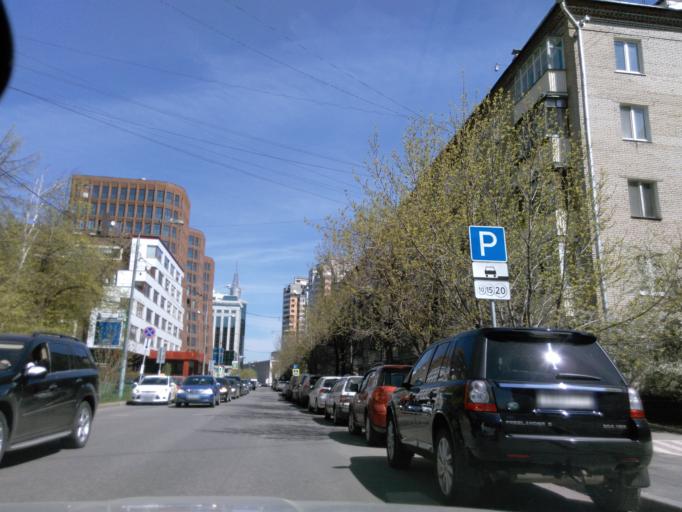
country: RU
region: Moscow
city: Luzhniki
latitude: 55.7239
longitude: 37.5724
